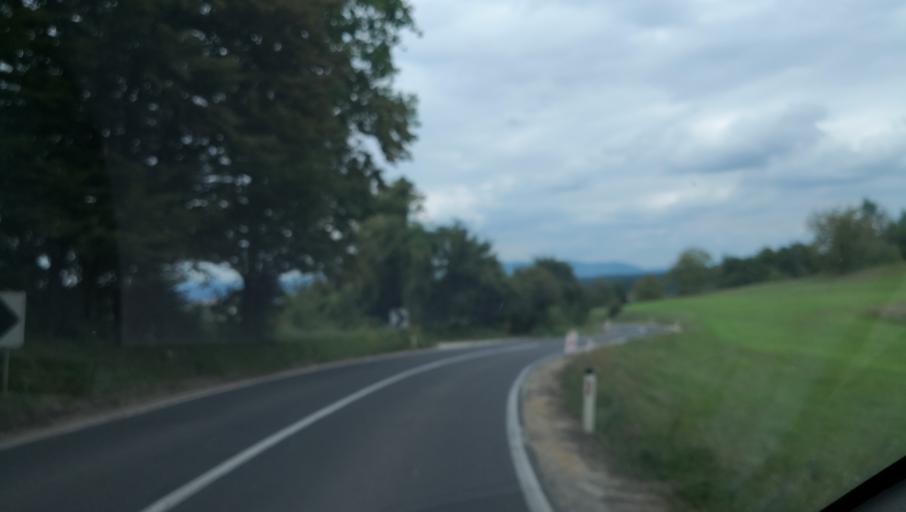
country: SI
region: Novo Mesto
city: Novo Mesto
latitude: 45.7636
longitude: 15.1963
